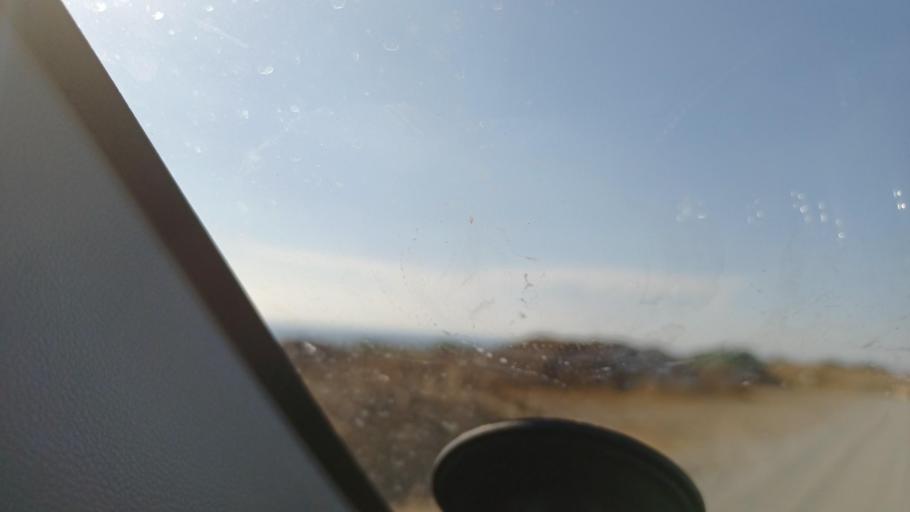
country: CY
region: Pafos
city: Mesogi
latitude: 34.7350
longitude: 32.5494
